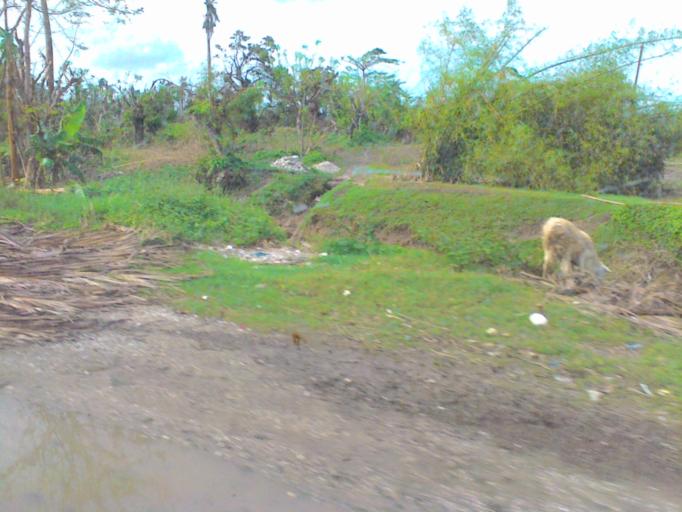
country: HT
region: Sud
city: Les Cayes
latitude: 18.2234
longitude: -73.7697
